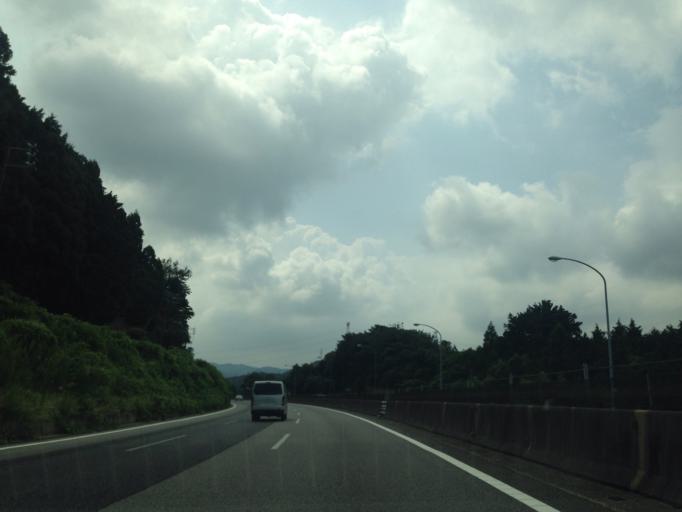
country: JP
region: Aichi
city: Gamagori
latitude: 34.8854
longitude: 137.2659
